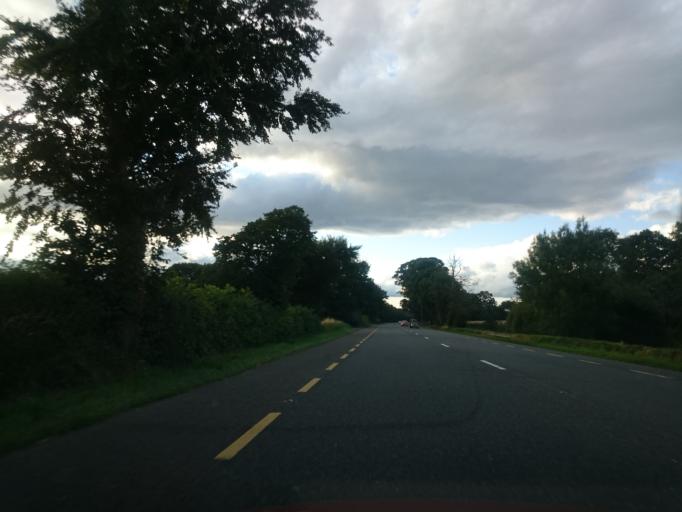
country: IE
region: Leinster
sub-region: Loch Garman
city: Enniscorthy
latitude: 52.4591
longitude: -6.5582
